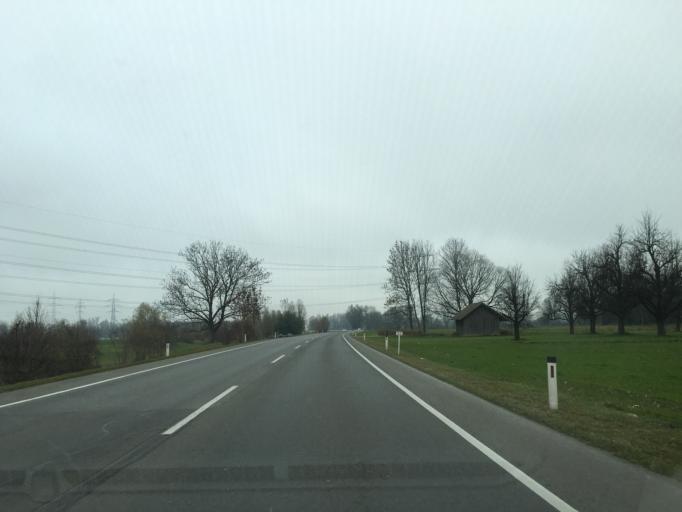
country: AT
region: Vorarlberg
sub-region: Politischer Bezirk Dornbirn
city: Hohenems
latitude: 47.3846
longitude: 9.6822
